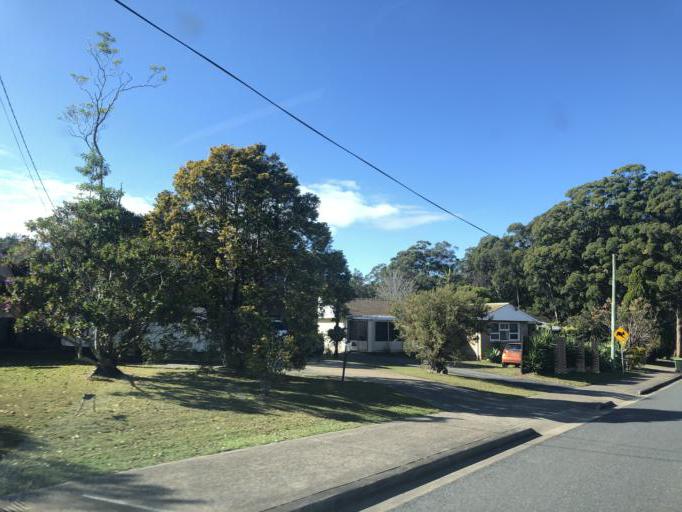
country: AU
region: New South Wales
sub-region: Coffs Harbour
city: Toormina
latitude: -30.3428
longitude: 153.0846
